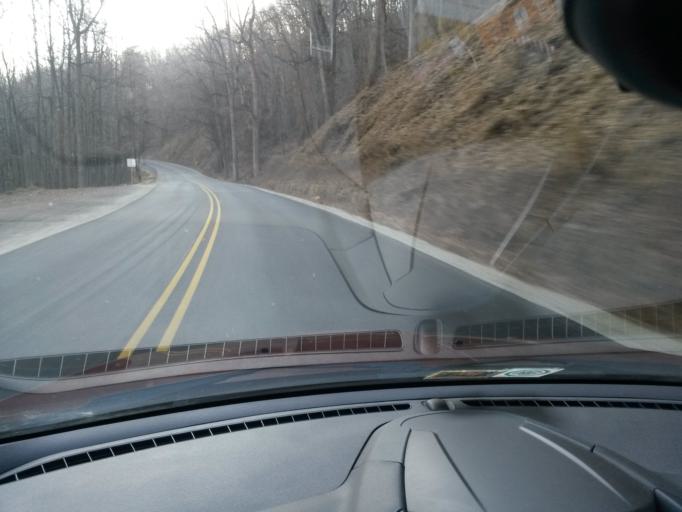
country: US
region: Virginia
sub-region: City of Buena Vista
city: Buena Vista
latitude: 37.7490
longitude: -79.2963
